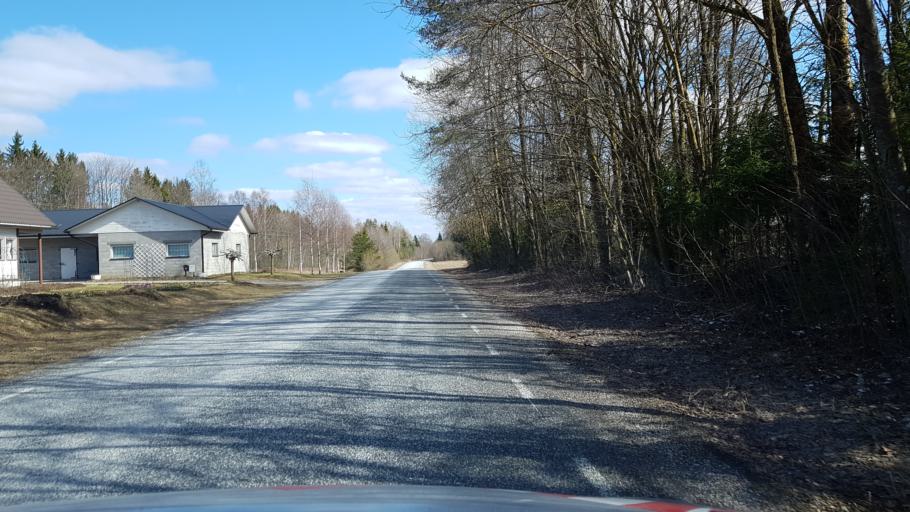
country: EE
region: Laeaene-Virumaa
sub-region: Tapa vald
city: Tapa
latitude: 59.2539
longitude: 25.7142
